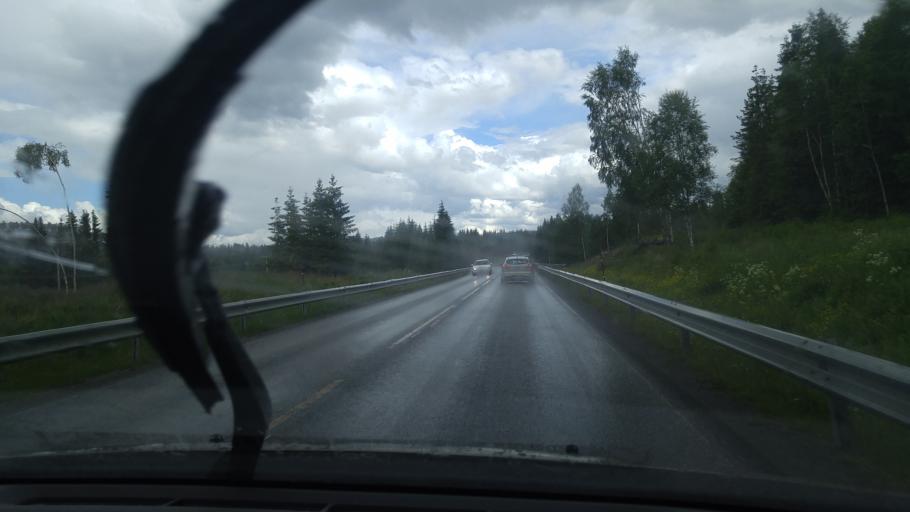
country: NO
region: Nord-Trondelag
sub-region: Namsos
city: Namsos
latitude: 64.4042
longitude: 11.4373
